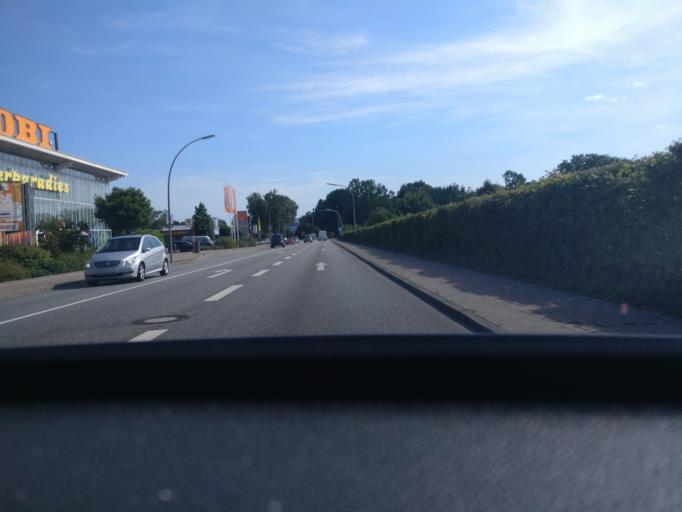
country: DE
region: Schleswig-Holstein
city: Norderstedt
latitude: 53.6685
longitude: 9.9709
